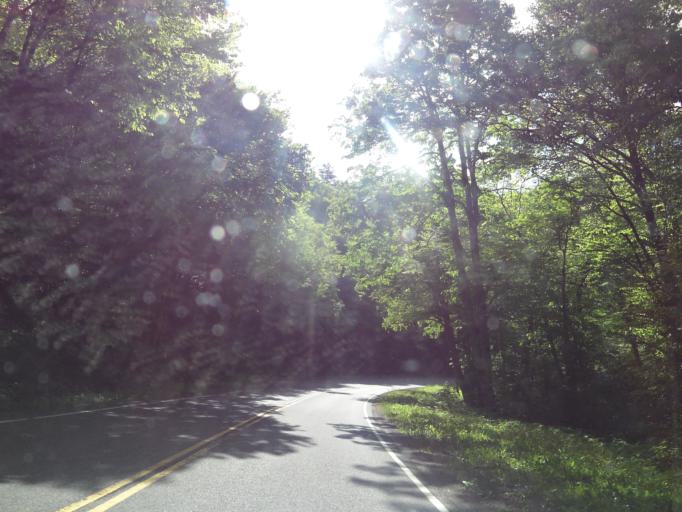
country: US
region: Tennessee
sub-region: Sevier County
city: Gatlinburg
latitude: 35.6211
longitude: -83.4376
